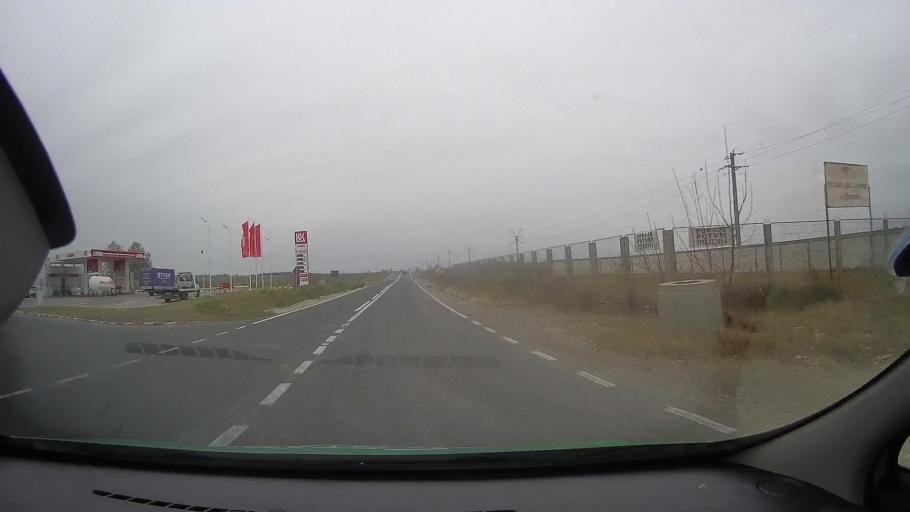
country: RO
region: Constanta
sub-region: Oras Harsova
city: Harsova
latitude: 44.6916
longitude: 27.9397
